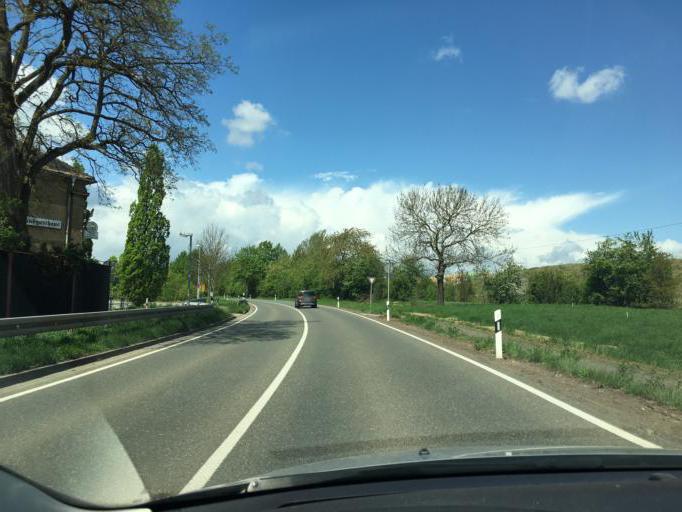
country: DE
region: Saxony
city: Frohburg
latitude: 51.0783
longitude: 12.5438
